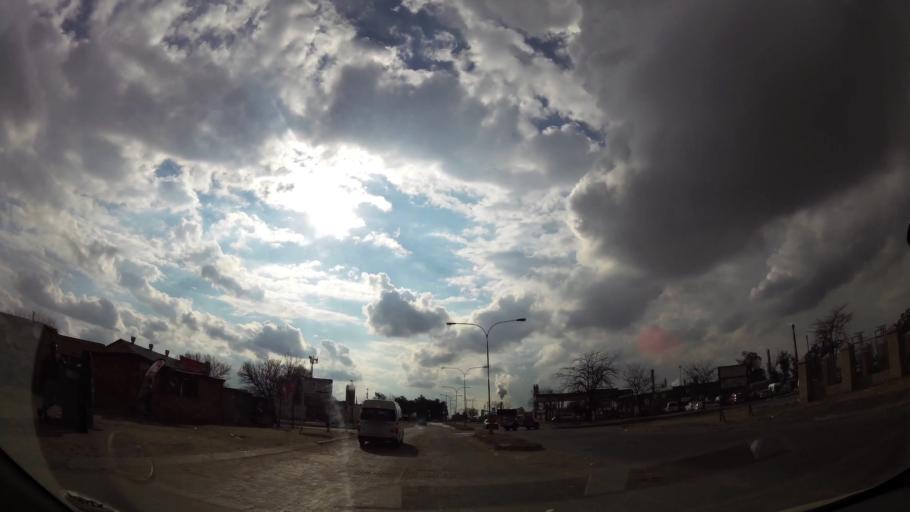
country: ZA
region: Orange Free State
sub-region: Fezile Dabi District Municipality
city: Sasolburg
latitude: -26.8371
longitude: 27.8434
